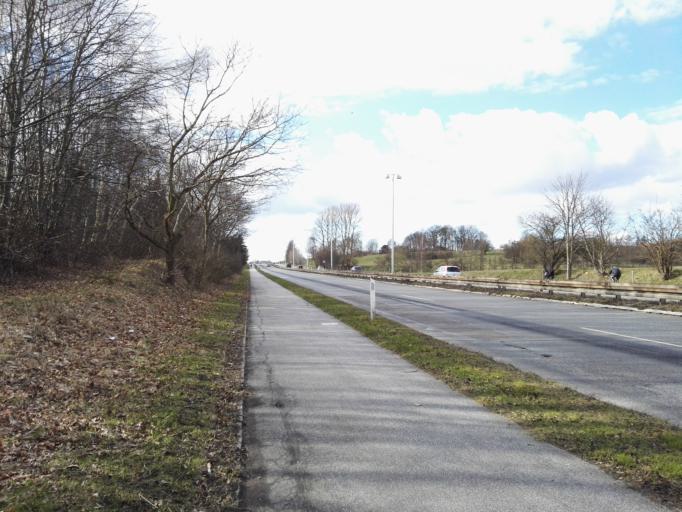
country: DK
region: Capital Region
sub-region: Ballerup Kommune
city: Malov
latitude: 55.7414
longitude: 12.3377
